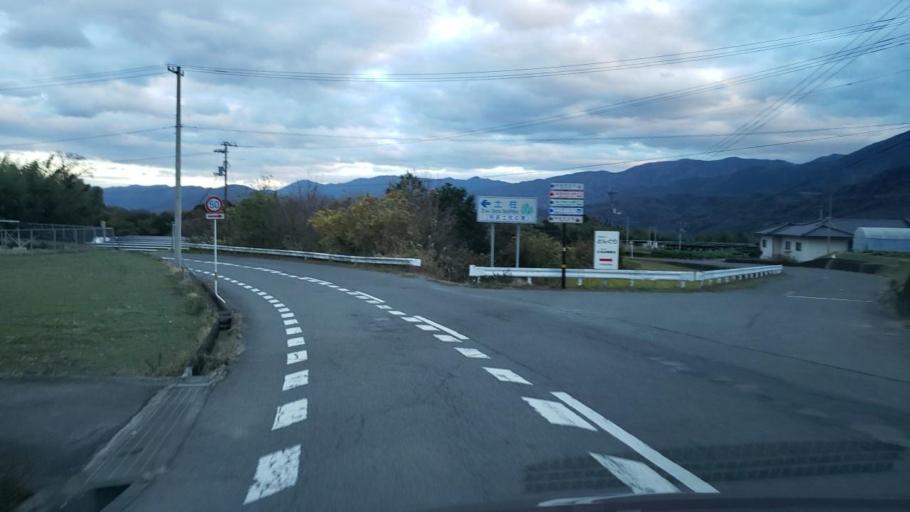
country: JP
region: Tokushima
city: Wakimachi
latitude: 34.0834
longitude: 134.1885
